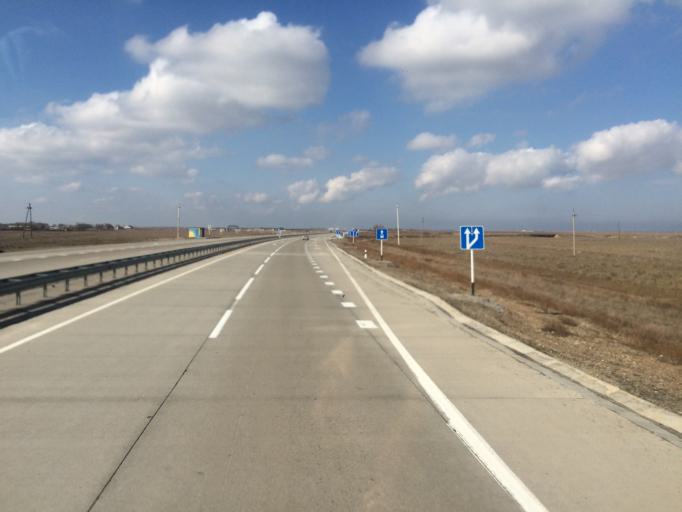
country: KZ
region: Ongtustik Qazaqstan
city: Temirlanovka
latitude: 42.8554
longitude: 69.0738
